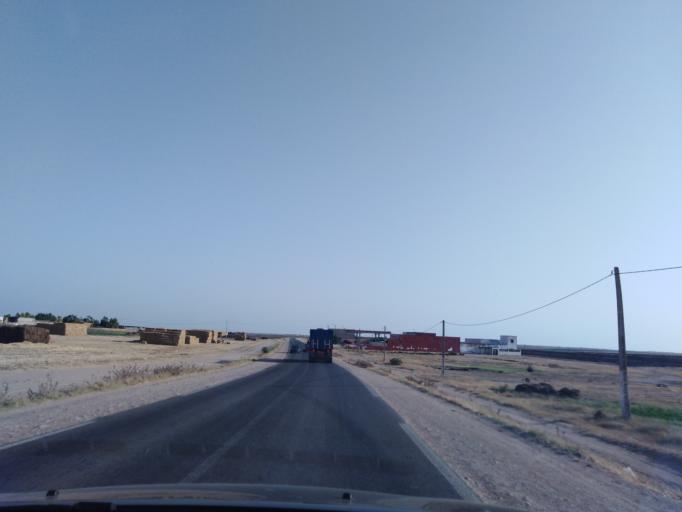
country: MA
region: Doukkala-Abda
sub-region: El-Jadida
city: Sidi Bennour
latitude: 32.5419
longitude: -8.7276
